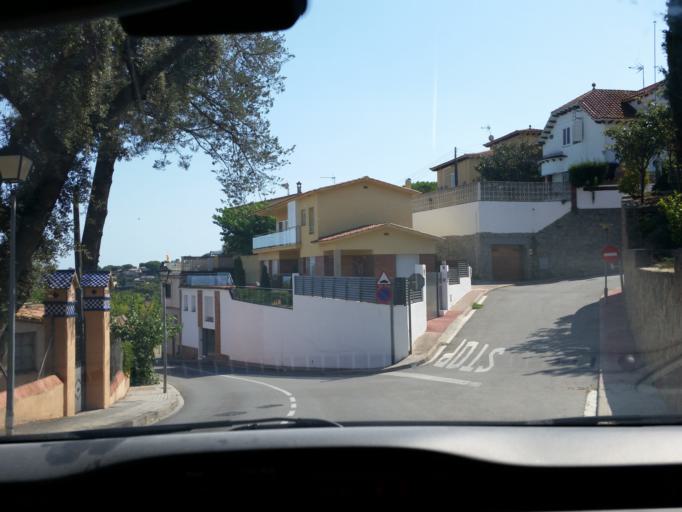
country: ES
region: Catalonia
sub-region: Provincia de Barcelona
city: Cabrils
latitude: 41.5291
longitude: 2.3657
